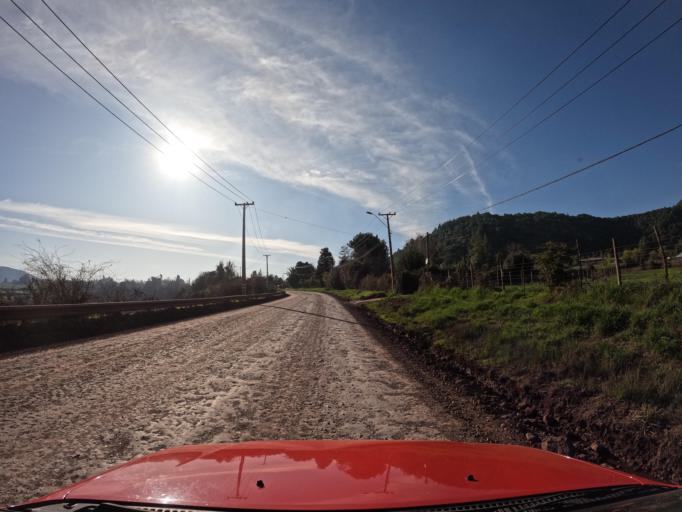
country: CL
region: Maule
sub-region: Provincia de Curico
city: Teno
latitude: -34.9638
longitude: -70.9539
